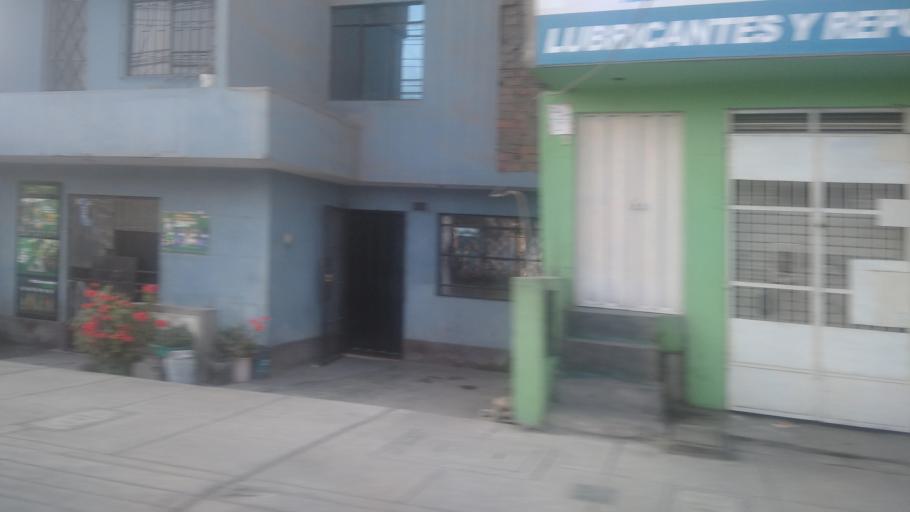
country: PE
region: Lima
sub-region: Lima
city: Vitarte
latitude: -12.0234
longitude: -76.9659
